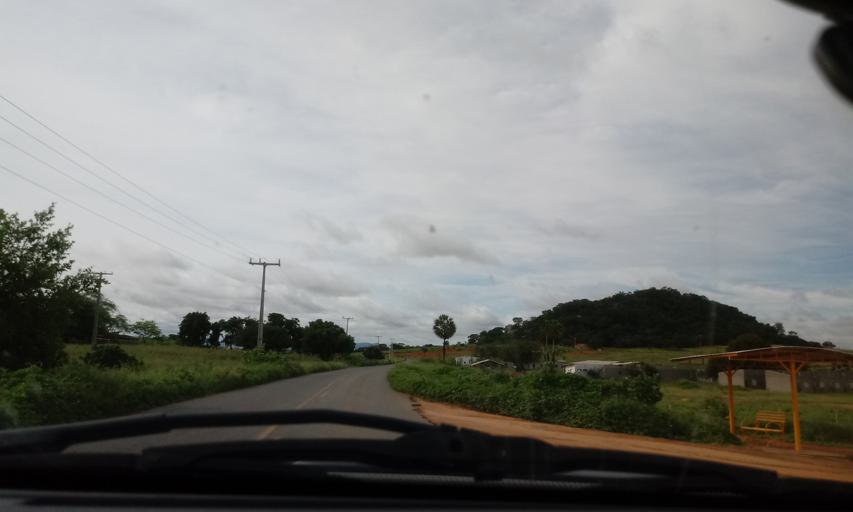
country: BR
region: Bahia
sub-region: Guanambi
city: Guanambi
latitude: -14.1356
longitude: -42.8483
